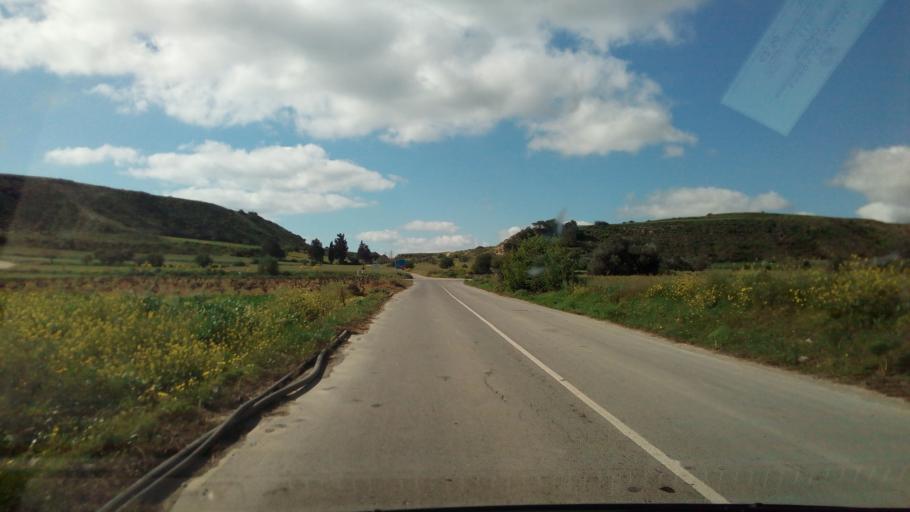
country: CY
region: Larnaka
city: Kofinou
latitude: 34.8073
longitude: 33.4660
